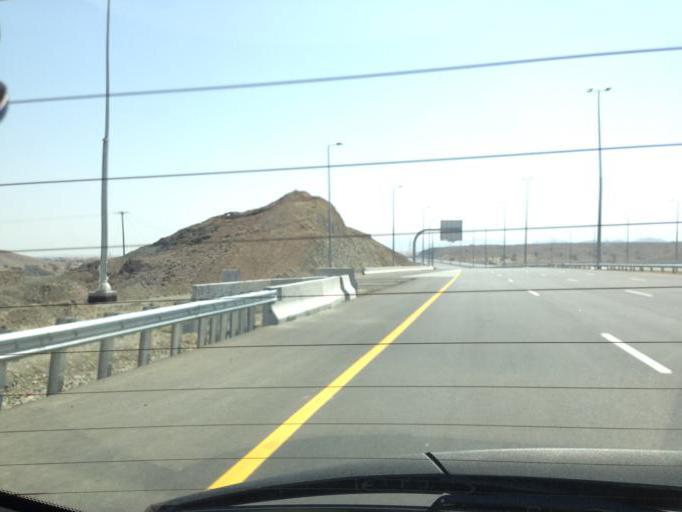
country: OM
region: Al Batinah
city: Rustaq
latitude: 23.5438
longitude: 57.5163
